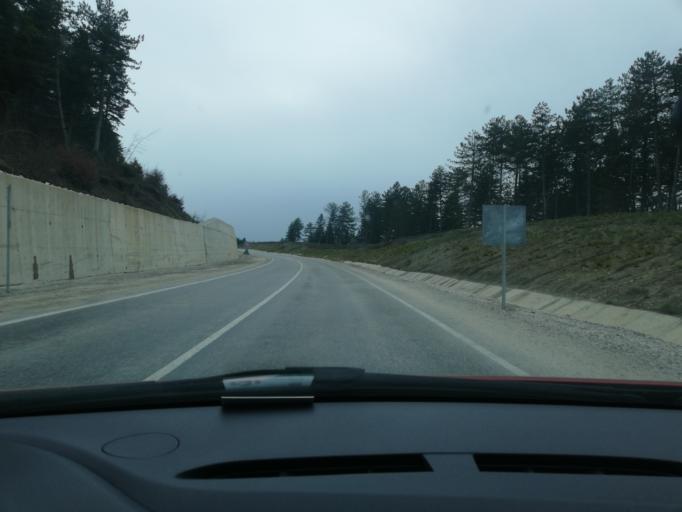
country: TR
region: Kastamonu
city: Pinarbasi
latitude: 41.5704
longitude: 33.0966
